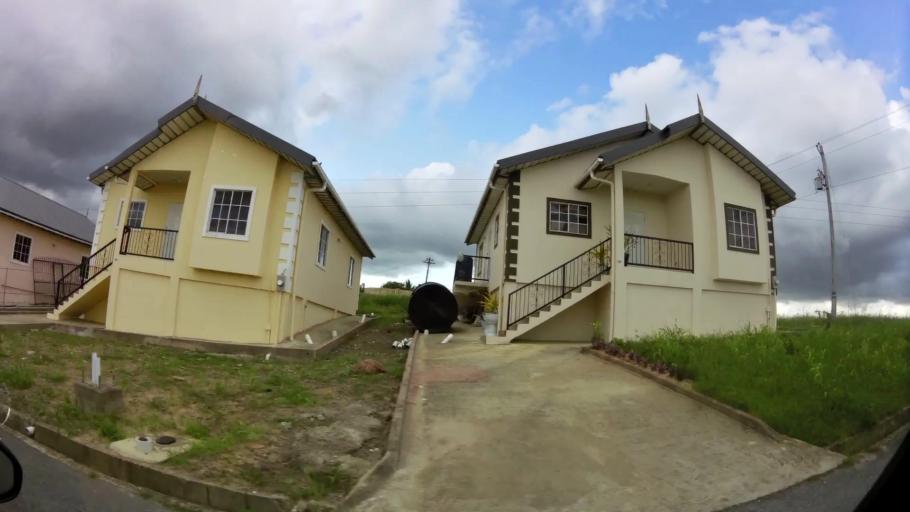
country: TT
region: City of San Fernando
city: Mon Repos
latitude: 10.2512
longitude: -61.4535
